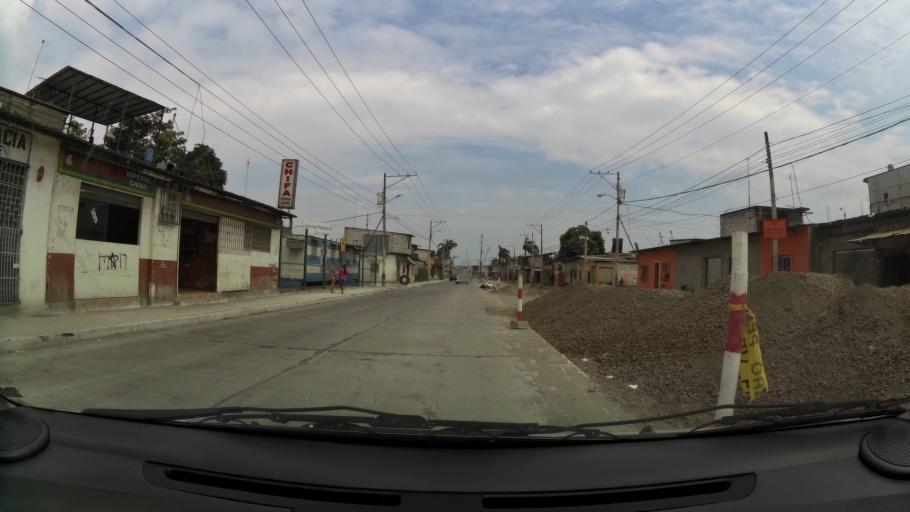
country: EC
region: Guayas
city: Guayaquil
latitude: -2.2431
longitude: -79.9254
